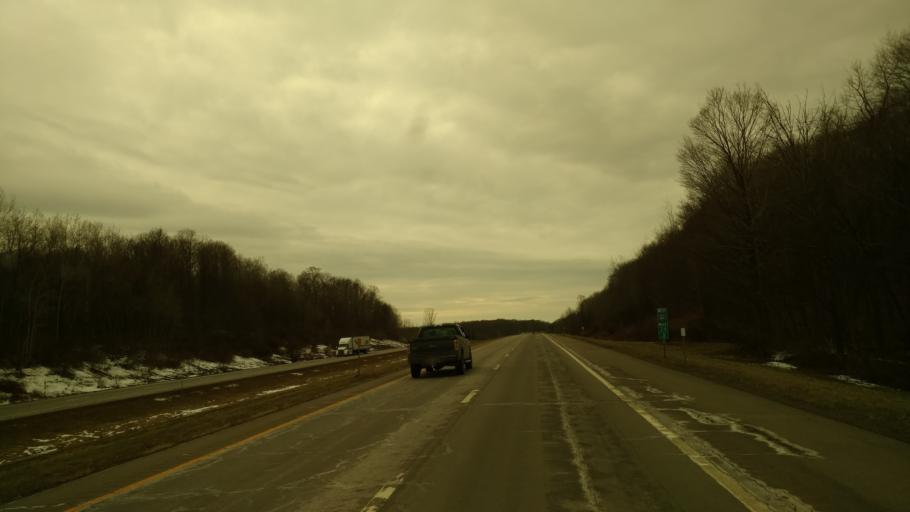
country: US
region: New York
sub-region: Chautauqua County
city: Celoron
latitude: 42.1284
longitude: -79.3000
